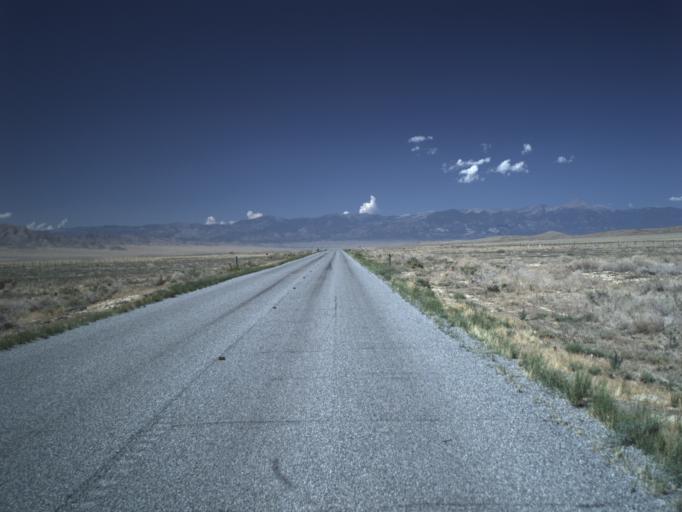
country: US
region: Utah
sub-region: Beaver County
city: Milford
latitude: 39.0619
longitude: -113.7521
